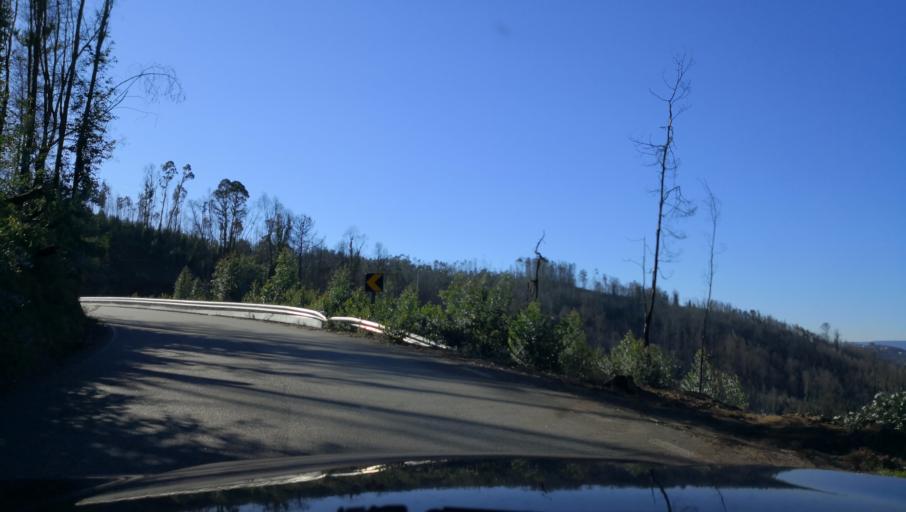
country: PT
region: Viseu
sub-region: Vouzela
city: Vouzela
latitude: 40.7282
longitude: -8.1278
